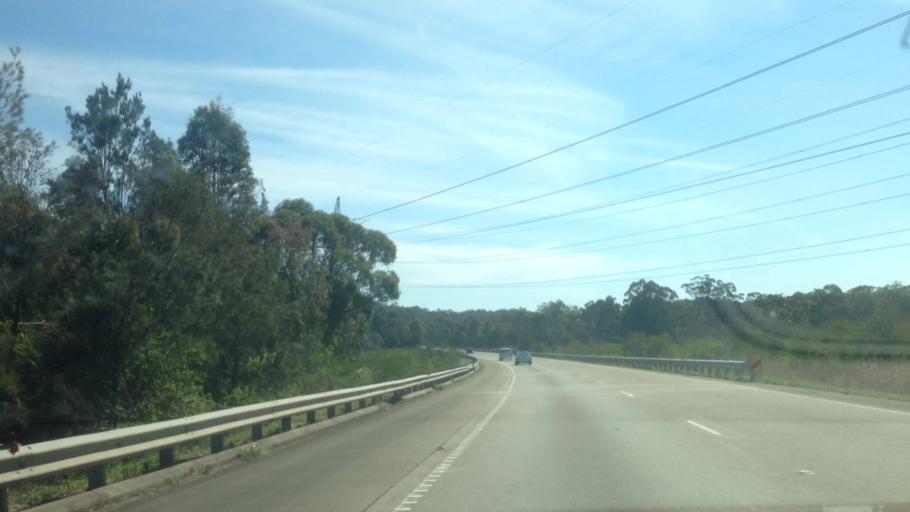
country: AU
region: New South Wales
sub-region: Lake Macquarie Shire
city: Fennell Bay
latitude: -32.9552
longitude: 151.5441
